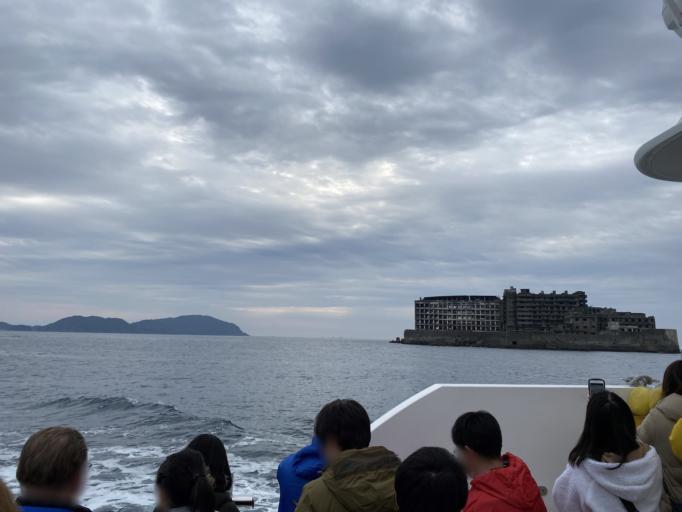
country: JP
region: Nagasaki
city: Nagasaki-shi
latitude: 32.6323
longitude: 129.7402
